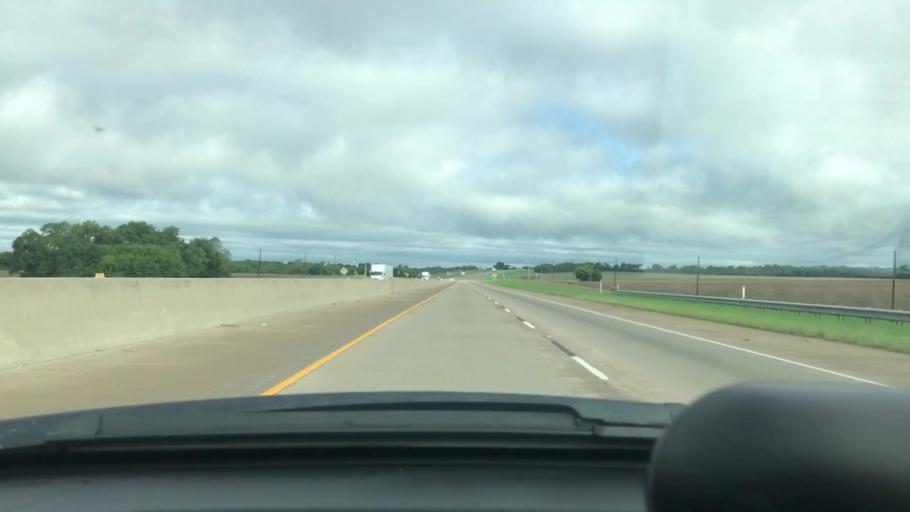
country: US
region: Texas
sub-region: Grayson County
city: Howe
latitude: 33.4669
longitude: -96.6136
